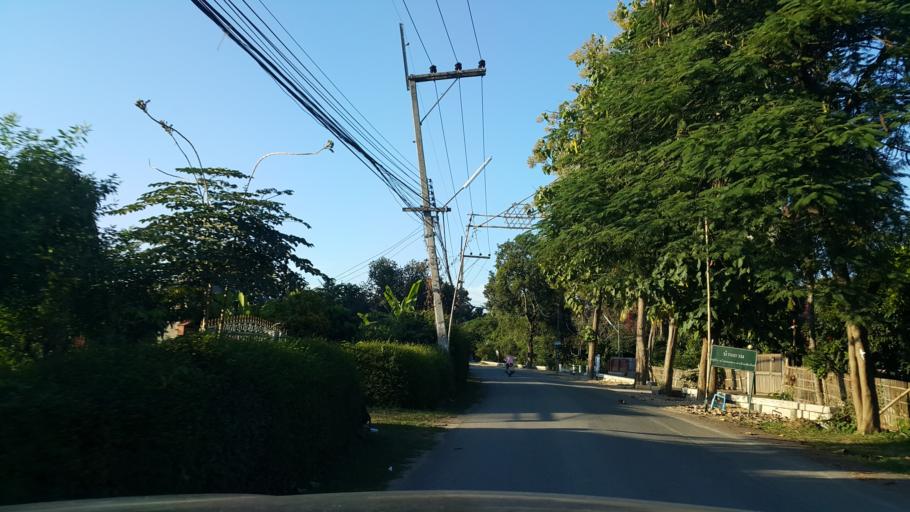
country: TH
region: Chiang Mai
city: Saraphi
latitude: 18.7520
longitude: 99.0495
